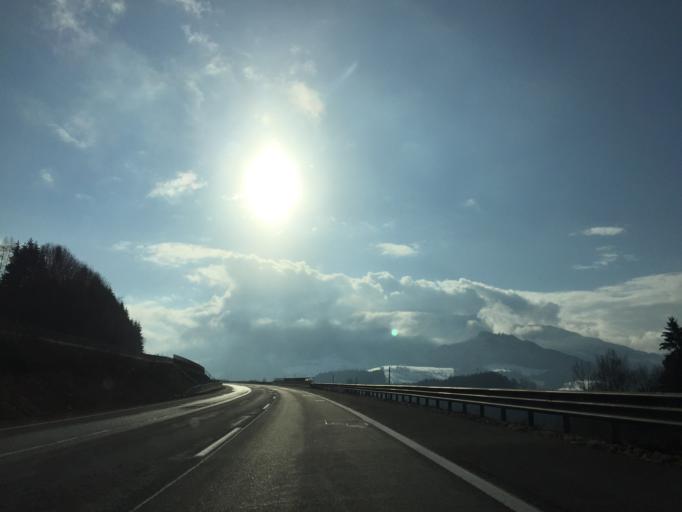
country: AT
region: Salzburg
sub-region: Politischer Bezirk Sankt Johann im Pongau
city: Pfarrwerfen
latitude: 47.4409
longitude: 13.2213
